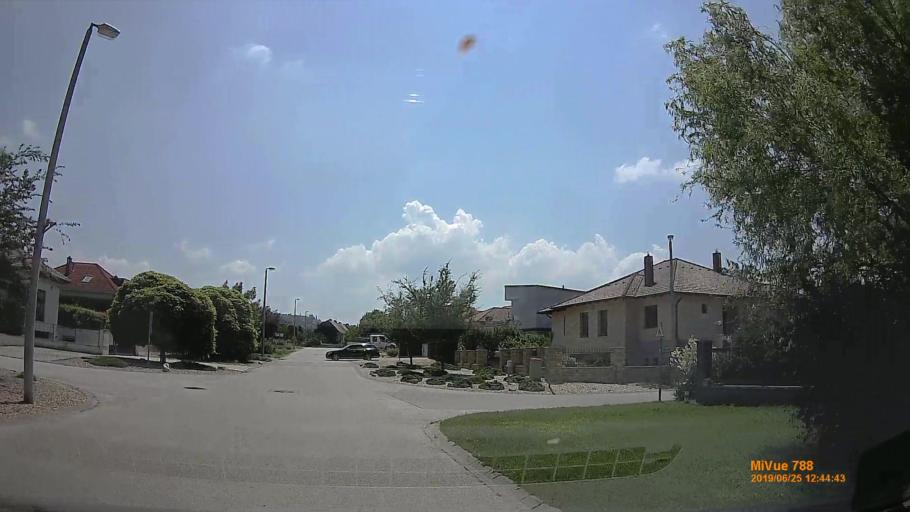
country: HU
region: Komarom-Esztergom
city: Esztergom
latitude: 47.8099
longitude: 18.7457
